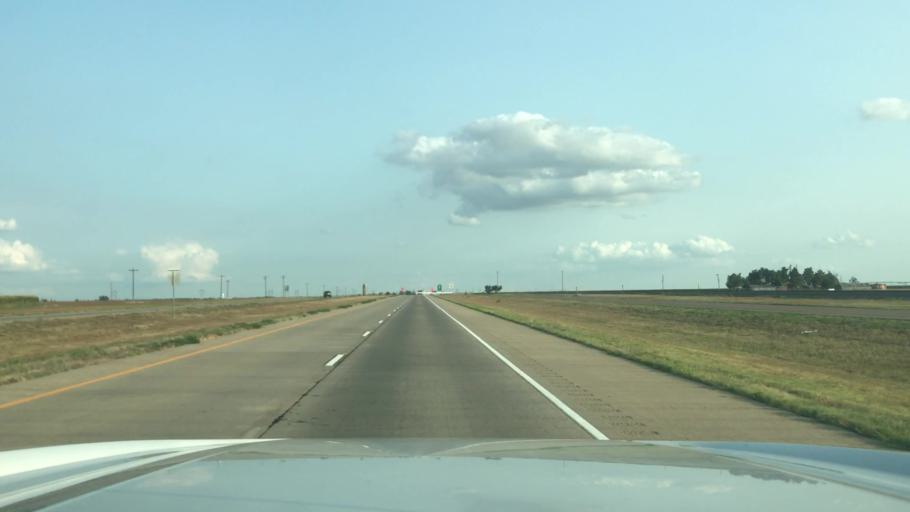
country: US
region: Texas
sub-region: Swisher County
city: Tulia
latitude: 34.5986
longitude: -101.8044
